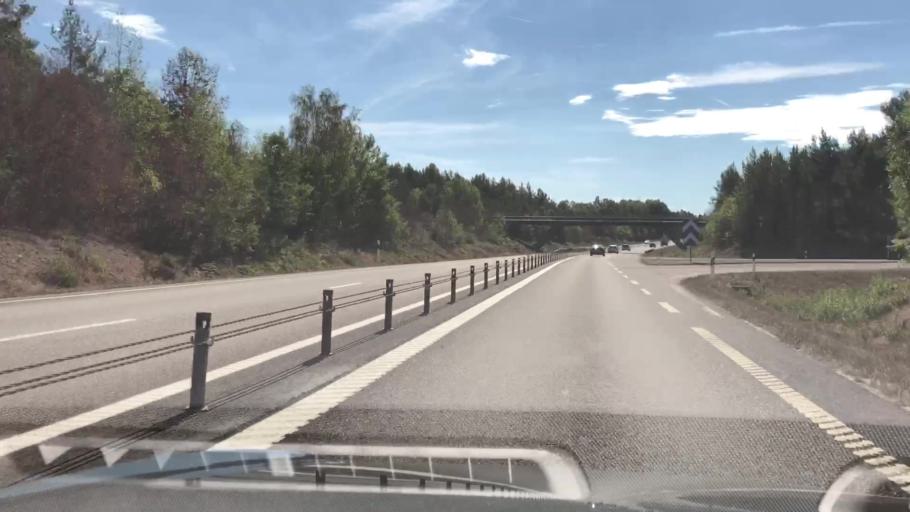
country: SE
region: Kalmar
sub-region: Oskarshamns Kommun
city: Paskallavik
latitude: 57.1527
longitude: 16.4617
